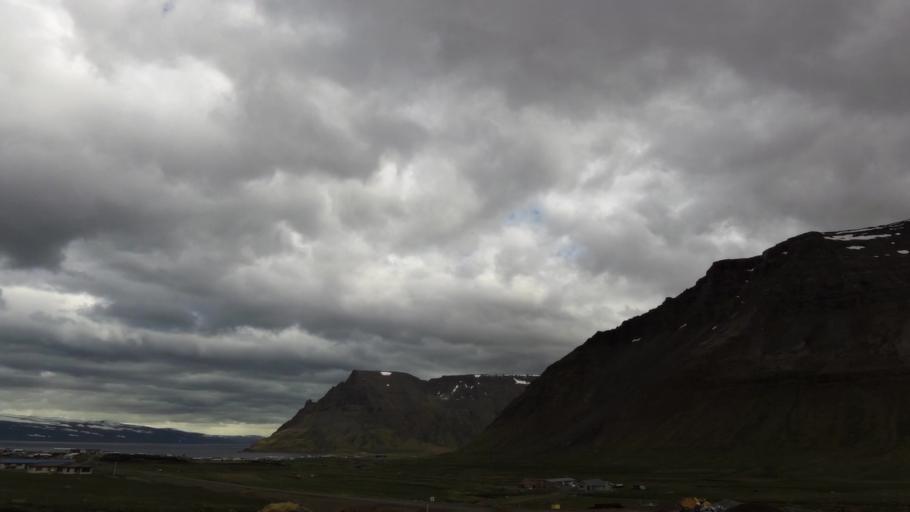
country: IS
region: Westfjords
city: Isafjoerdur
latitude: 66.1583
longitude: -23.2935
